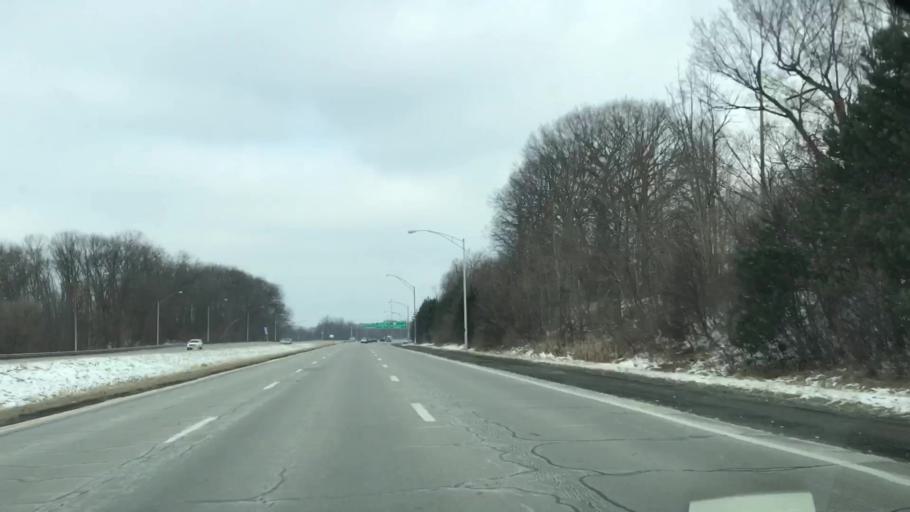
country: US
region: Ohio
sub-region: Mahoning County
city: Struthers
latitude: 41.0541
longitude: -80.6293
